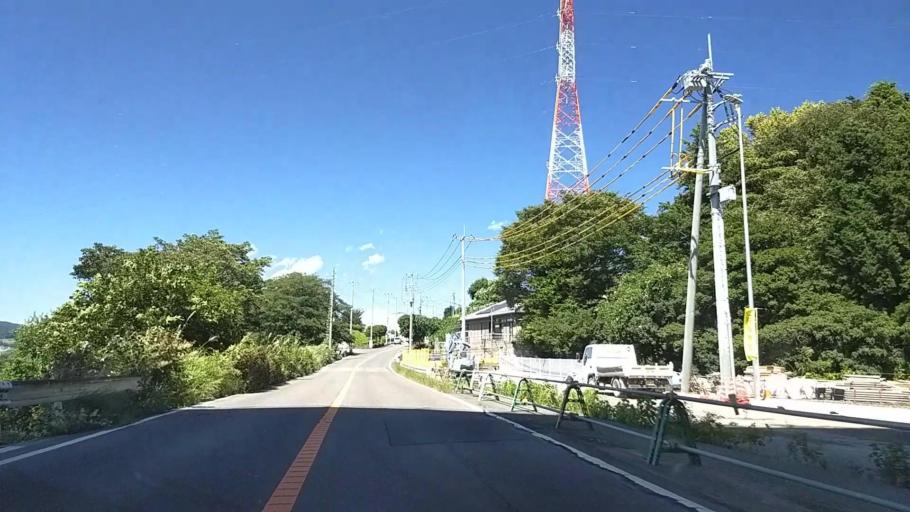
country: JP
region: Kanagawa
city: Zama
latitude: 35.5274
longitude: 139.3572
